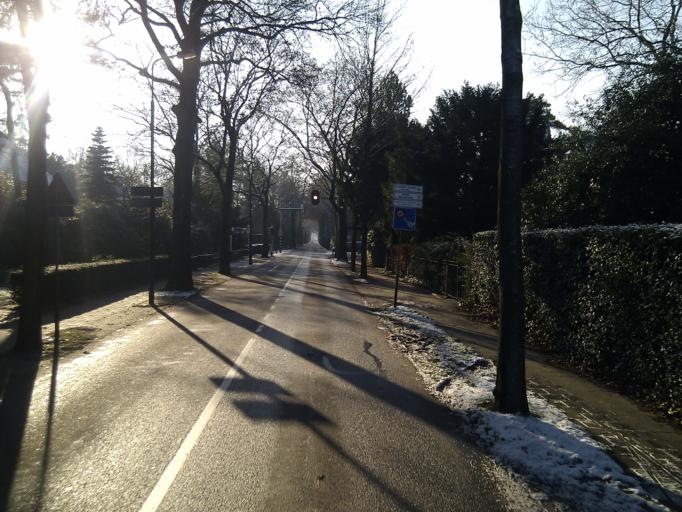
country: NL
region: Utrecht
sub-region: Gemeente De Bilt
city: De Bilt
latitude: 52.1362
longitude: 5.2101
